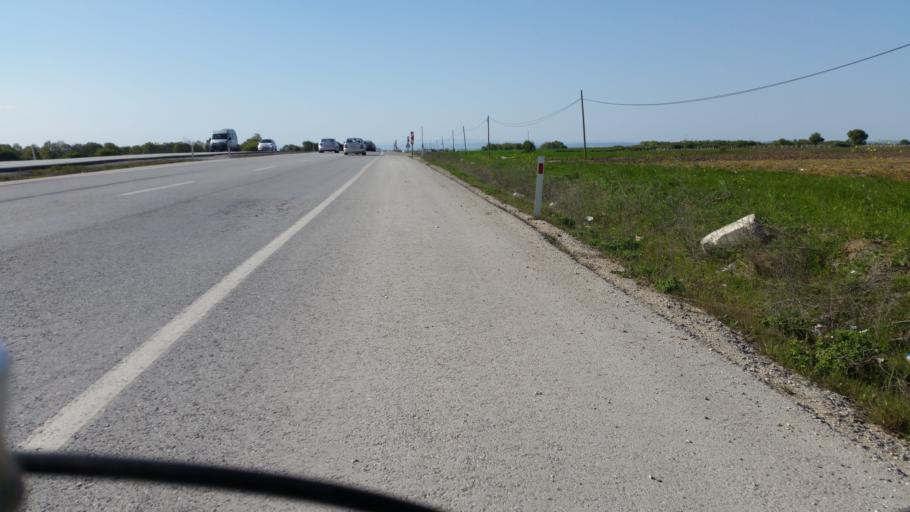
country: TR
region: Tekirdag
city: Cerkezkoey
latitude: 41.3424
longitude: 27.9639
